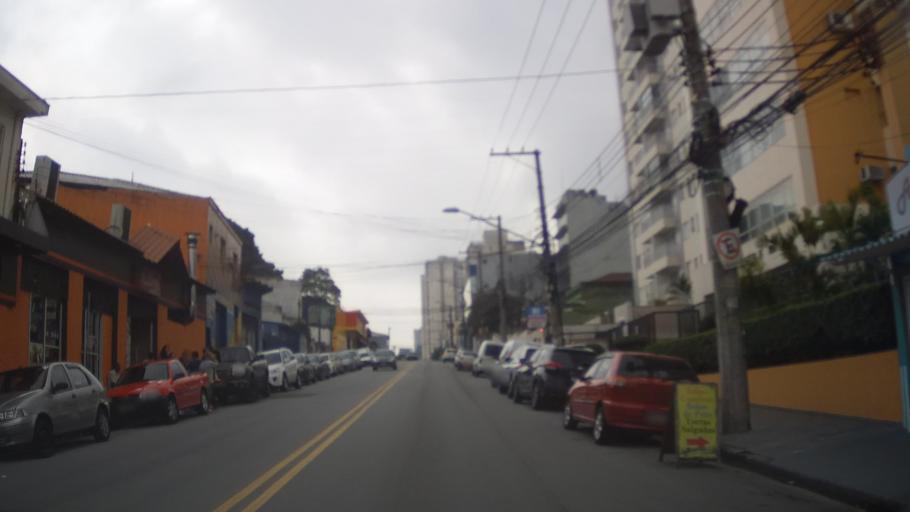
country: BR
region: Sao Paulo
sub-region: Guarulhos
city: Guarulhos
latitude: -23.4729
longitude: -46.5349
